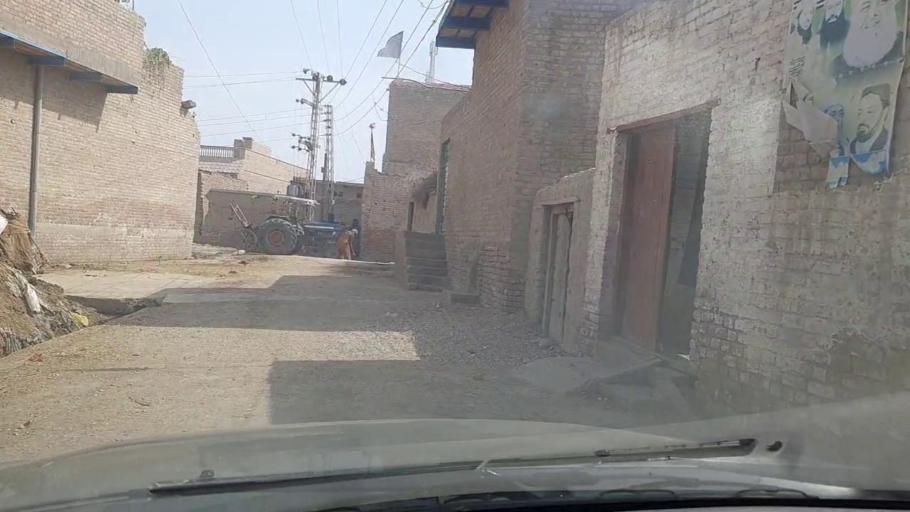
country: PK
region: Sindh
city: Chak
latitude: 27.8294
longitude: 68.7759
